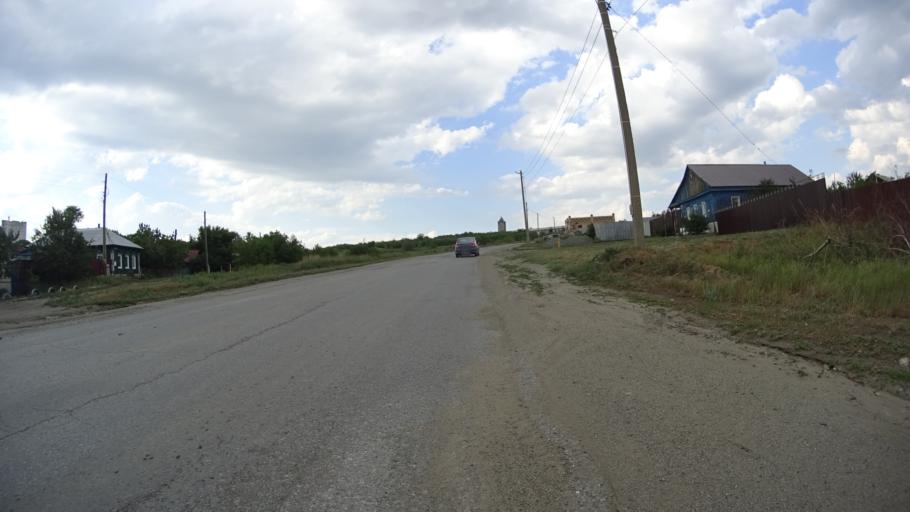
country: RU
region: Chelyabinsk
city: Troitsk
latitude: 54.0998
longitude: 61.5912
